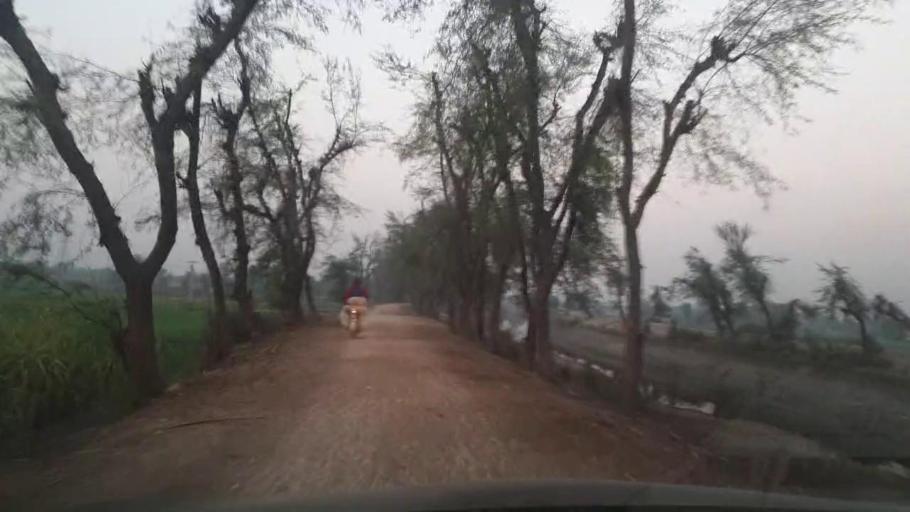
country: PK
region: Sindh
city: Ubauro
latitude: 28.1807
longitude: 69.7803
